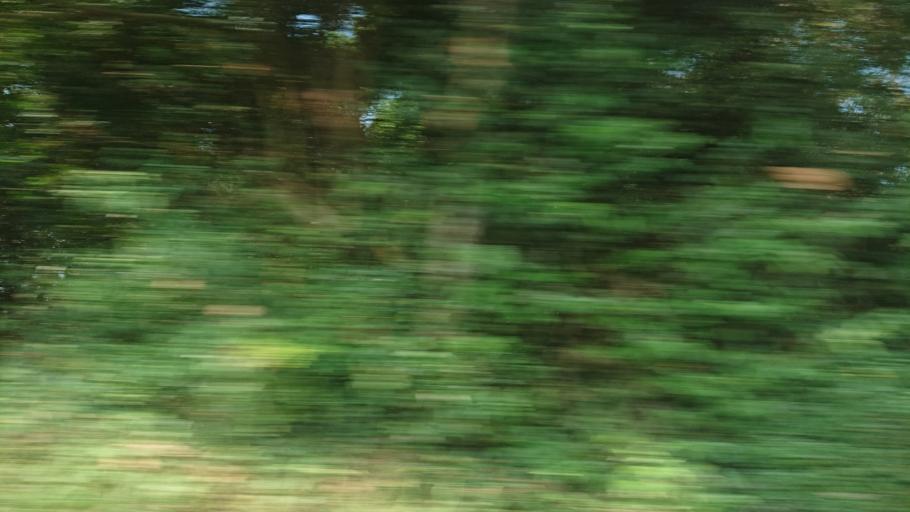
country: TW
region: Taiwan
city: Lugu
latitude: 23.7149
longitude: 120.6681
